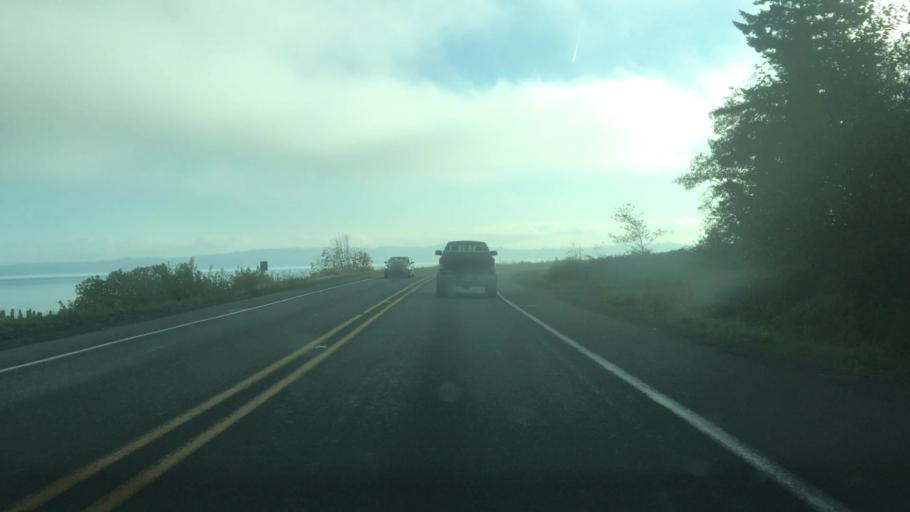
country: US
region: Oregon
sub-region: Clatsop County
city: Astoria
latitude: 46.2726
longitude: -123.8164
